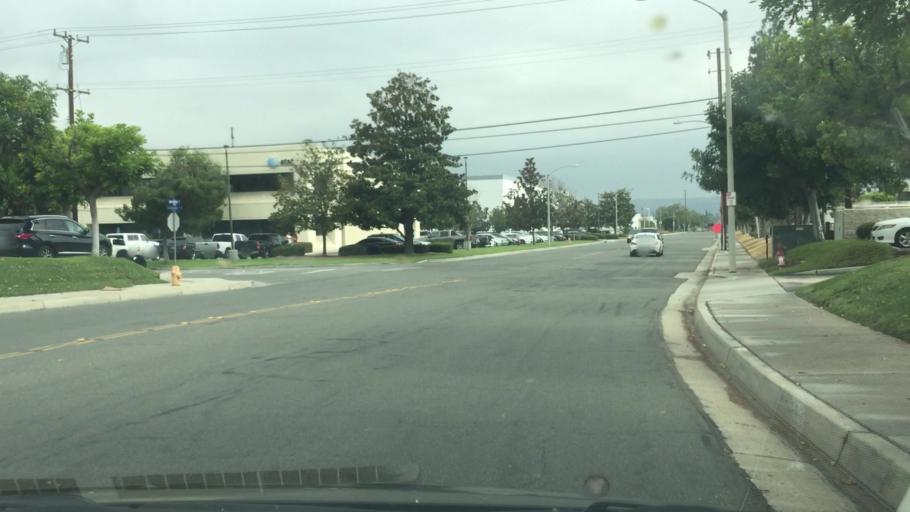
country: US
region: California
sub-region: Orange County
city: Yorba Linda
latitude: 33.8589
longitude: -117.8311
